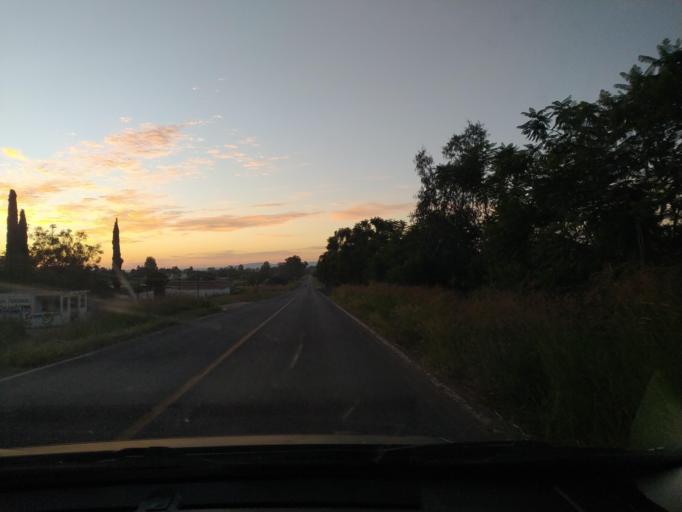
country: MX
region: Guanajuato
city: Ciudad Manuel Doblado
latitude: 20.8016
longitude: -101.9918
